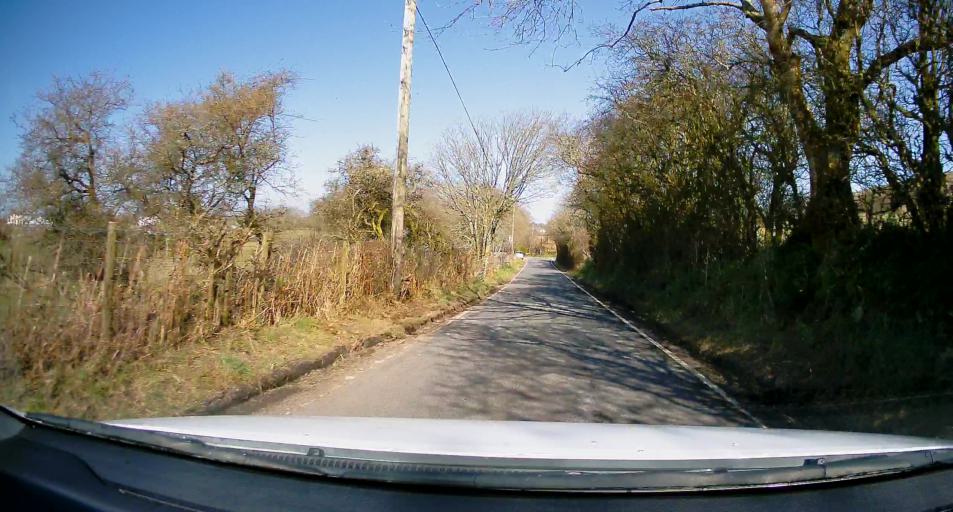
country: GB
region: Wales
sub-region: County of Ceredigion
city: Lledrod
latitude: 52.2820
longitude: -4.0605
